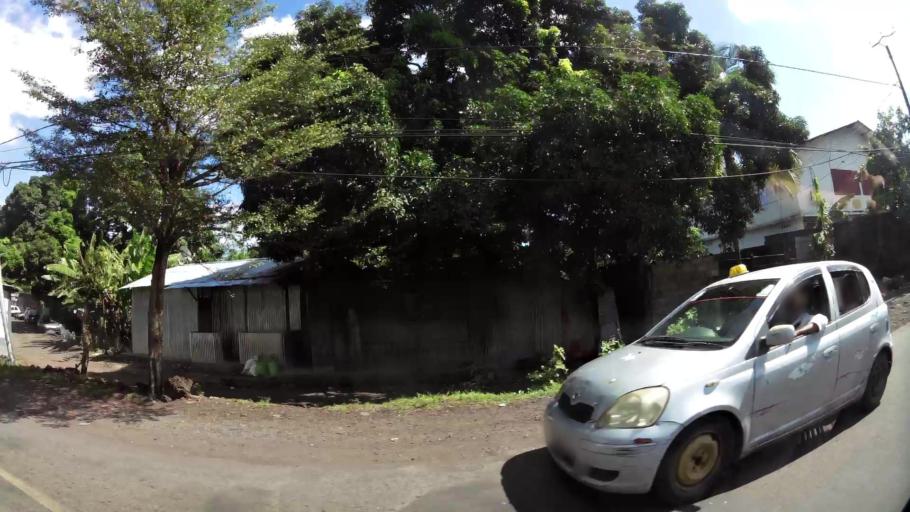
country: KM
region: Grande Comore
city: Mavingouni
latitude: -11.7215
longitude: 43.2506
